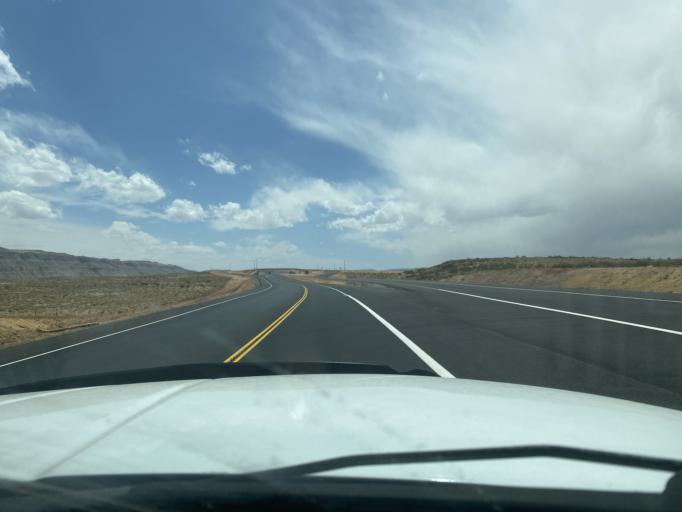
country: US
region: Utah
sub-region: Washington County
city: Hurricane
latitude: 37.1333
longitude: -113.3478
